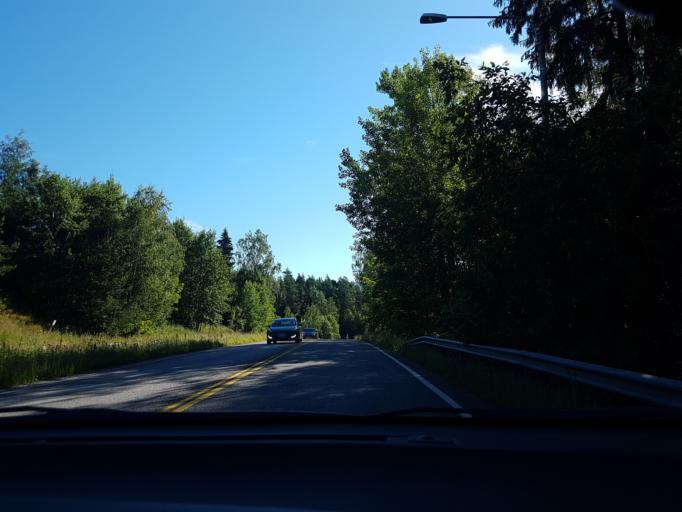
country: FI
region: Uusimaa
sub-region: Helsinki
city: Sibbo
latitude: 60.2605
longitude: 25.2241
